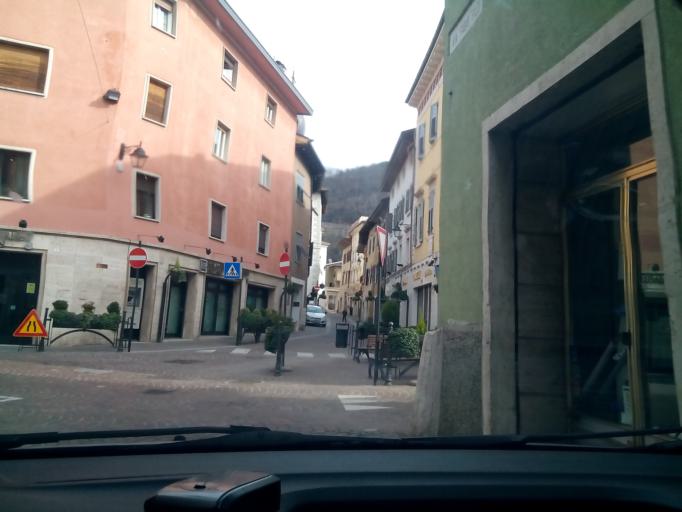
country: IT
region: Trentino-Alto Adige
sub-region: Provincia di Trento
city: Lavis
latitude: 46.1385
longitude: 11.1134
